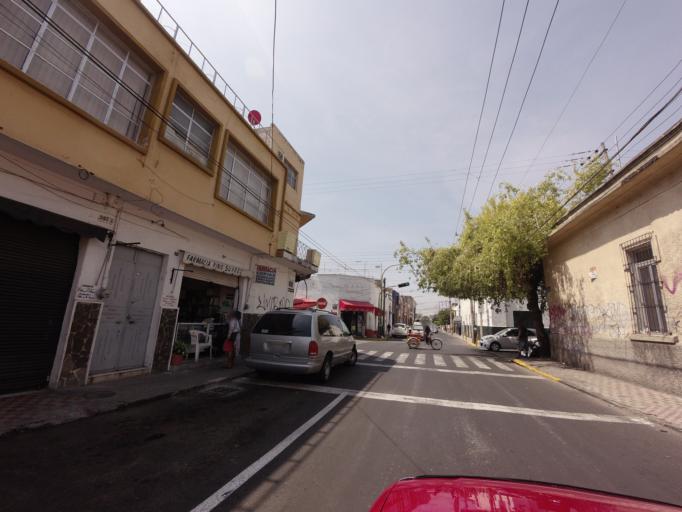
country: MX
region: Jalisco
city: Guadalajara
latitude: 20.6857
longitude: -103.3463
